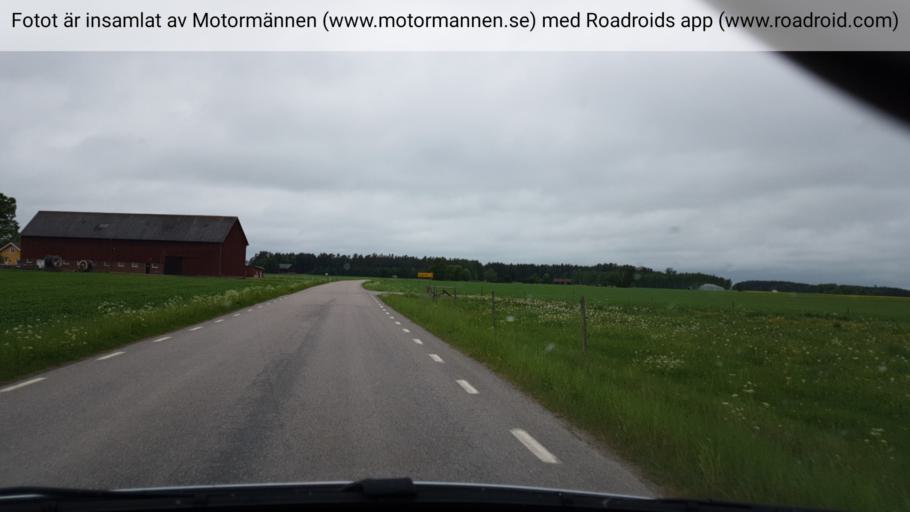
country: SE
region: Vaestra Goetaland
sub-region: Lidkopings Kommun
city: Vinninga
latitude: 58.4459
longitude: 13.3382
